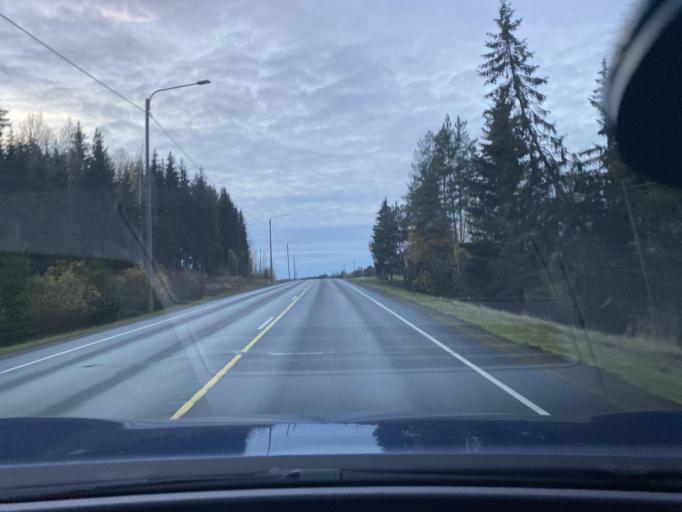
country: FI
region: Uusimaa
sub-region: Helsinki
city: Saukkola
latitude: 60.3874
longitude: 24.0532
